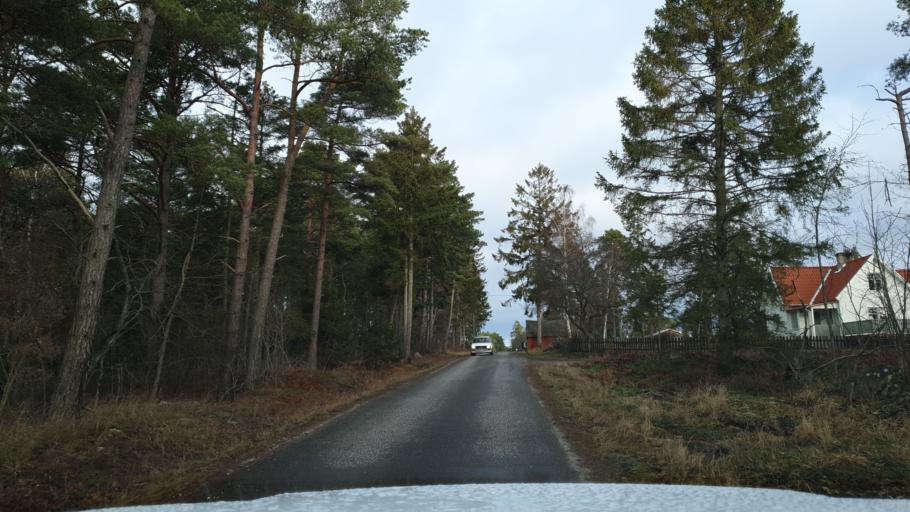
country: SE
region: Gotland
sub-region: Gotland
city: Slite
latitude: 57.3778
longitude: 18.8033
